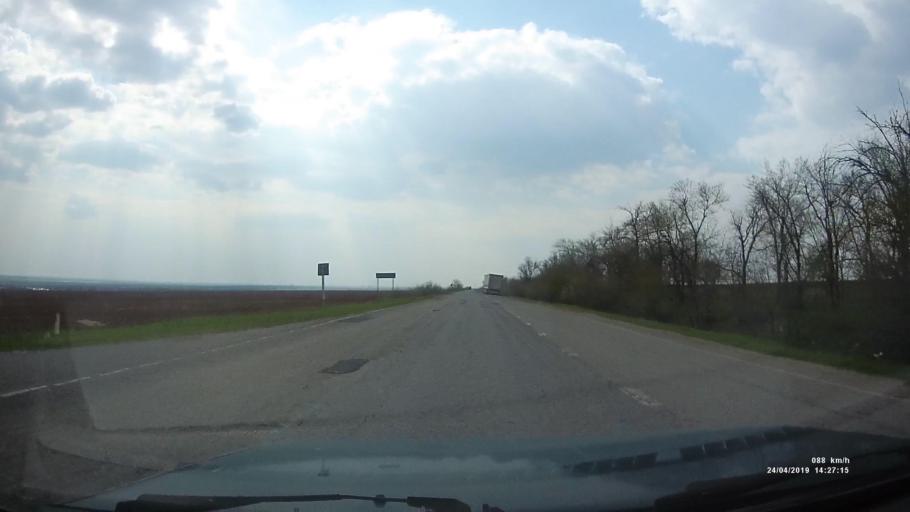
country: RU
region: Kalmykiya
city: Arshan'
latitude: 46.3340
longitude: 44.0467
